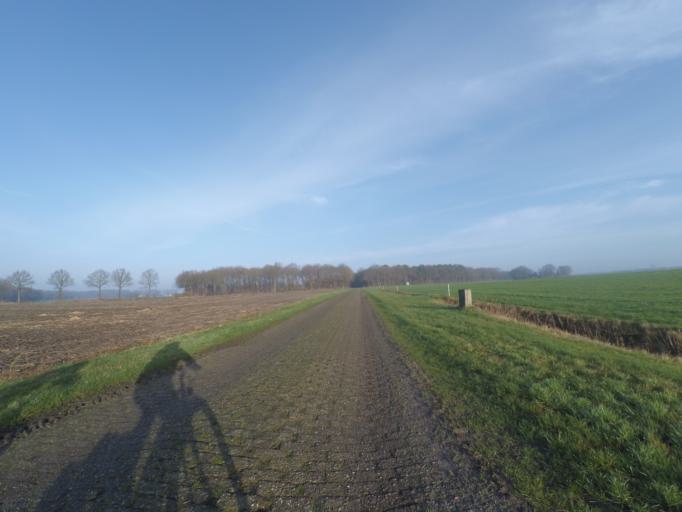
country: NL
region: Drenthe
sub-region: Gemeente Borger-Odoorn
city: Borger
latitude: 52.8970
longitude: 6.8019
